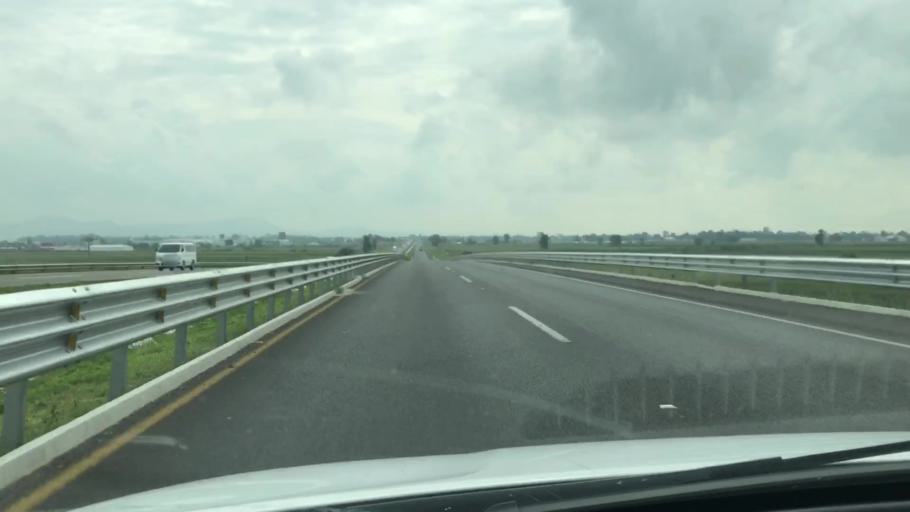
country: MX
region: Guanajuato
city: Irapuato
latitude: 20.6523
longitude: -101.3170
